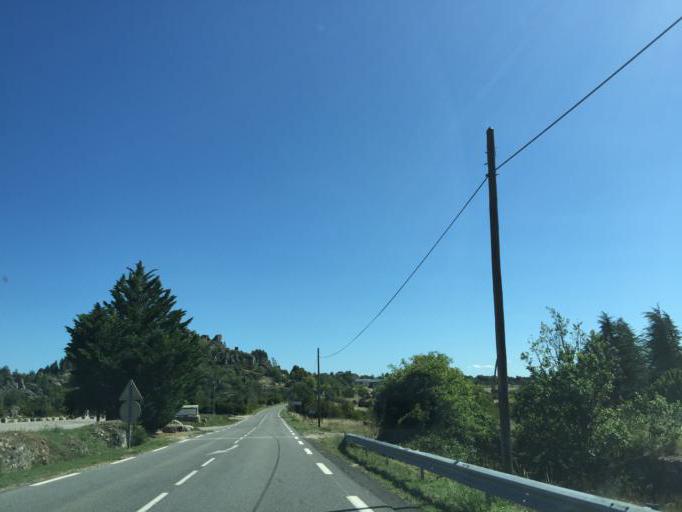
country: FR
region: Languedoc-Roussillon
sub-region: Departement de l'Herault
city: Lodeve
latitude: 43.8705
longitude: 3.3139
